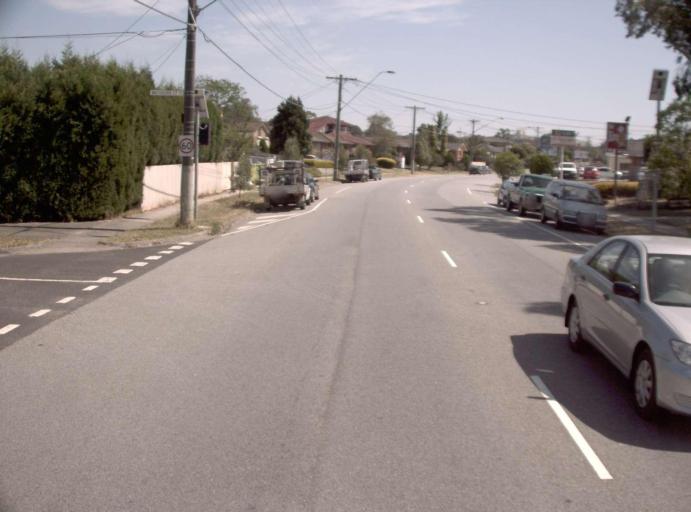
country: AU
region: Victoria
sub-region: Greater Dandenong
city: Noble Park North
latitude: -37.9473
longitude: 145.1917
